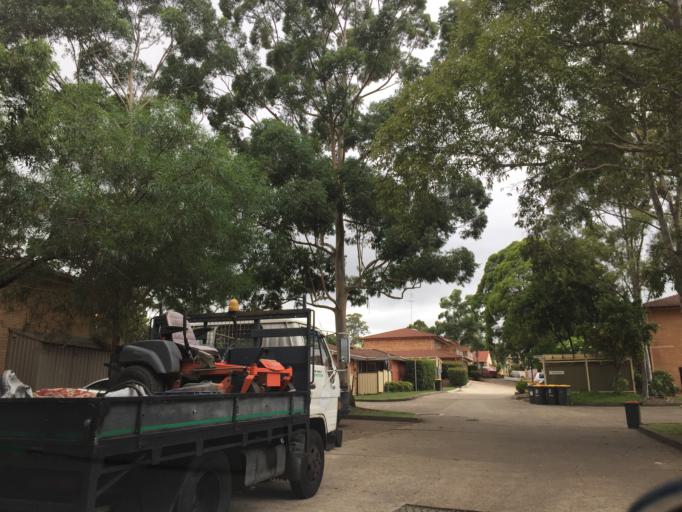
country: AU
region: New South Wales
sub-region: Blacktown
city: Blacktown
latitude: -33.7962
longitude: 150.8981
